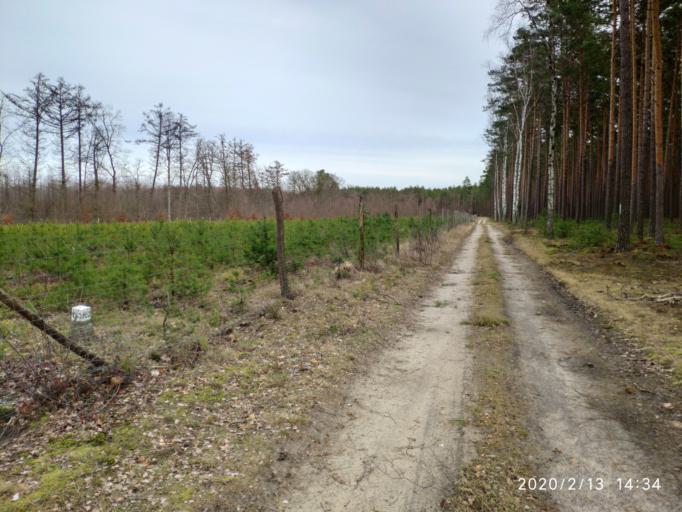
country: PL
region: Lubusz
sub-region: Powiat zielonogorski
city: Zabor
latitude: 51.9743
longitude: 15.6296
